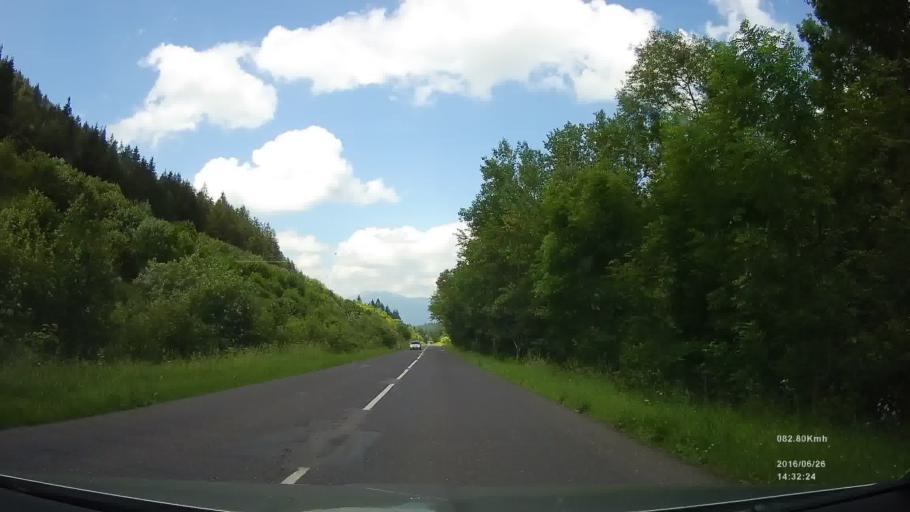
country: SK
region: Zilinsky
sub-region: Okres Zilina
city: Liptovsky Hradok
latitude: 49.0122
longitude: 19.7704
